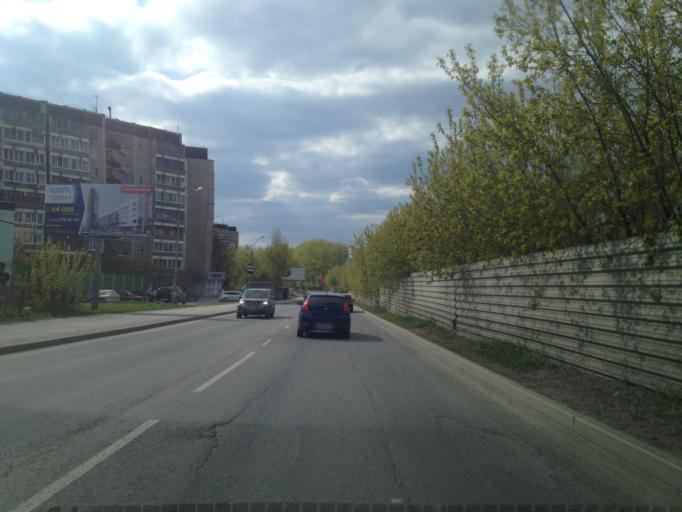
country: RU
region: Sverdlovsk
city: Yekaterinburg
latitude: 56.8562
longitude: 60.5743
